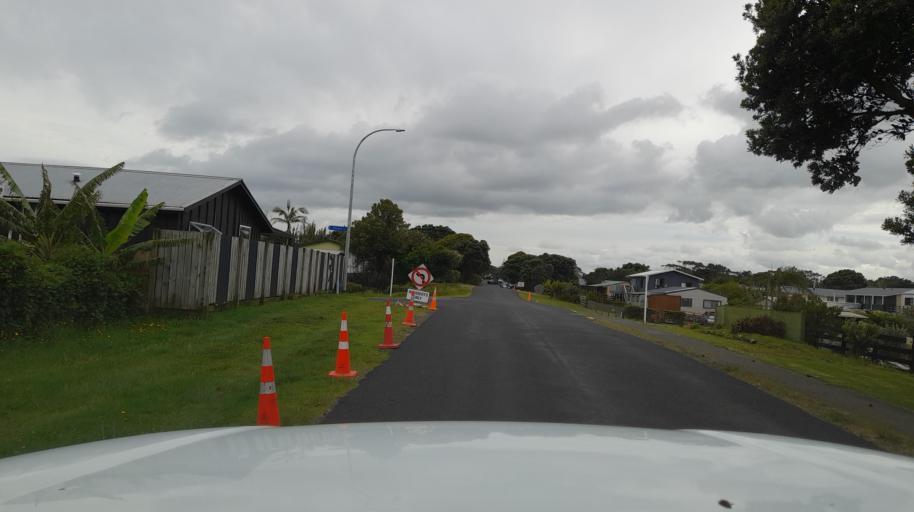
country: NZ
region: Northland
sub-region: Far North District
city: Ahipara
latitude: -35.1648
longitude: 173.1555
